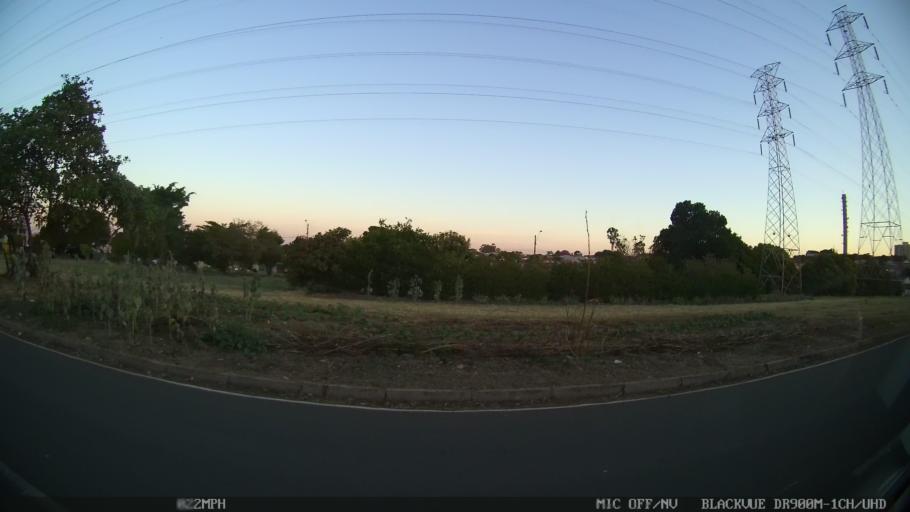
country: BR
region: Sao Paulo
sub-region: Sao Jose Do Rio Preto
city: Sao Jose do Rio Preto
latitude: -20.8440
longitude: -49.3815
